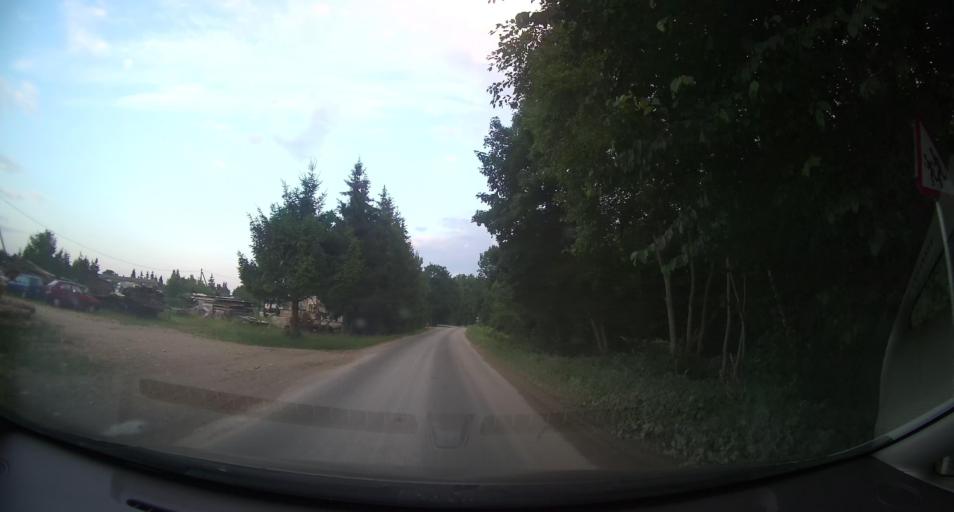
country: EE
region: Laeaene
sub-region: Lihula vald
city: Lihula
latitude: 58.5638
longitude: 23.7210
